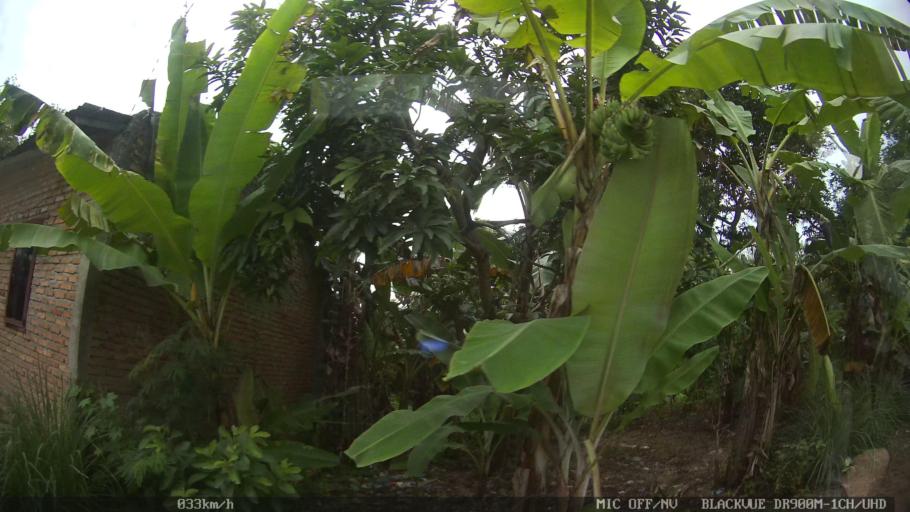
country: ID
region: North Sumatra
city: Sunggal
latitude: 3.6448
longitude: 98.5924
